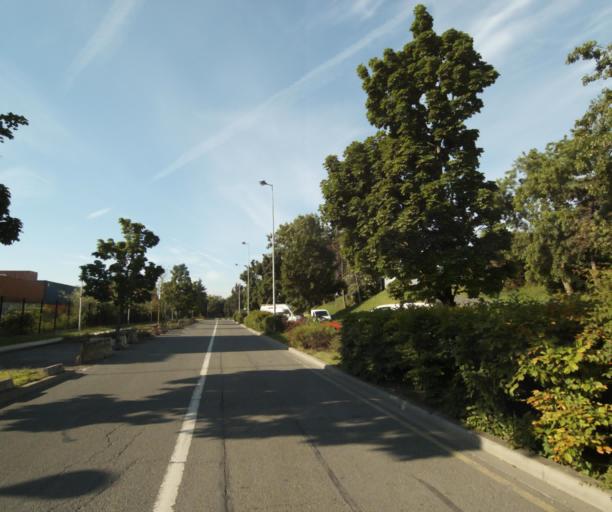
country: FR
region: Ile-de-France
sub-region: Departement du Val-d'Oise
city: Argenteuil
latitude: 48.9395
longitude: 2.2639
